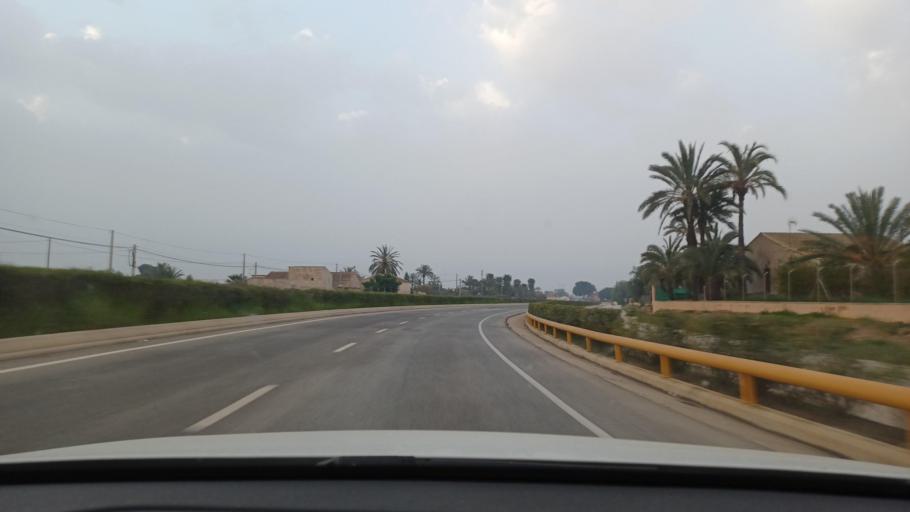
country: ES
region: Valencia
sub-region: Provincia de Alicante
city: Elche
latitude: 38.2196
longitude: -0.6973
